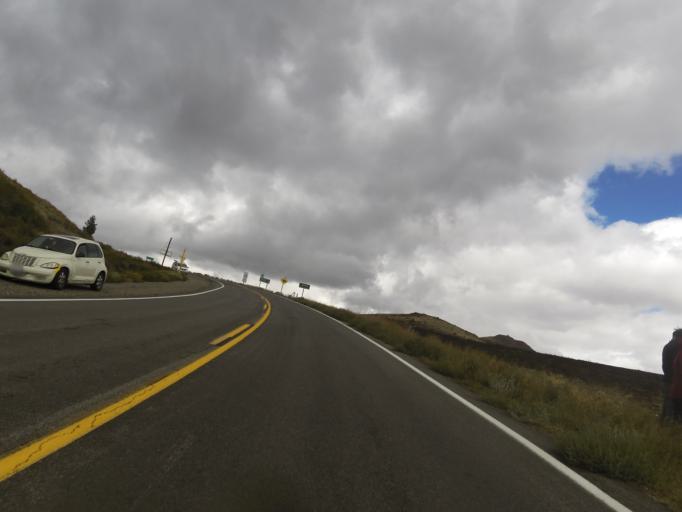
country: US
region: Nevada
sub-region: Douglas County
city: Gardnerville Ranchos
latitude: 38.6794
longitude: -119.5921
